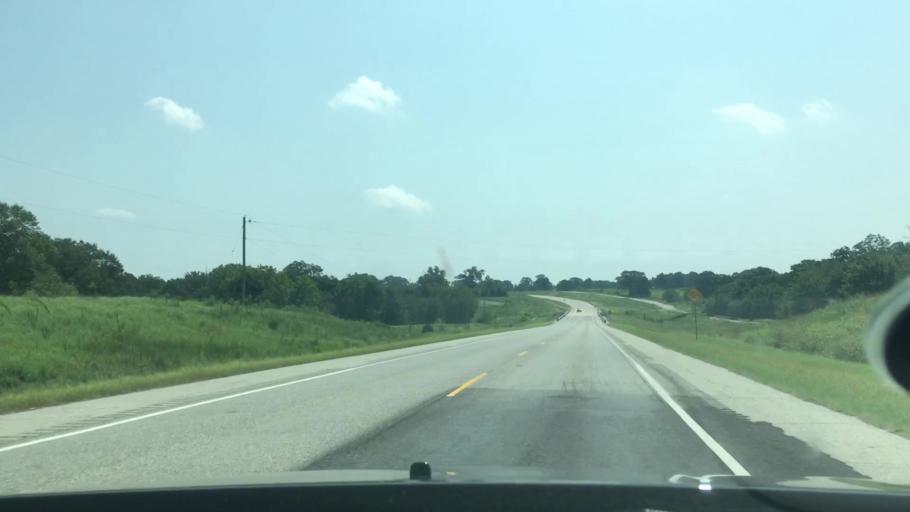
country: US
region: Oklahoma
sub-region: Atoka County
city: Atoka
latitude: 34.2930
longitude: -95.9756
